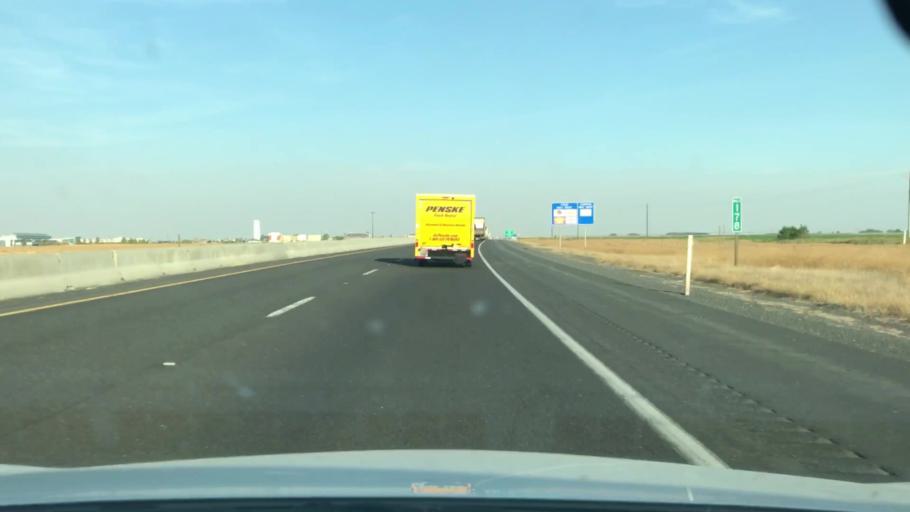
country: US
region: Washington
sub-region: Grant County
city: Moses Lake
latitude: 47.1024
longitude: -119.2733
